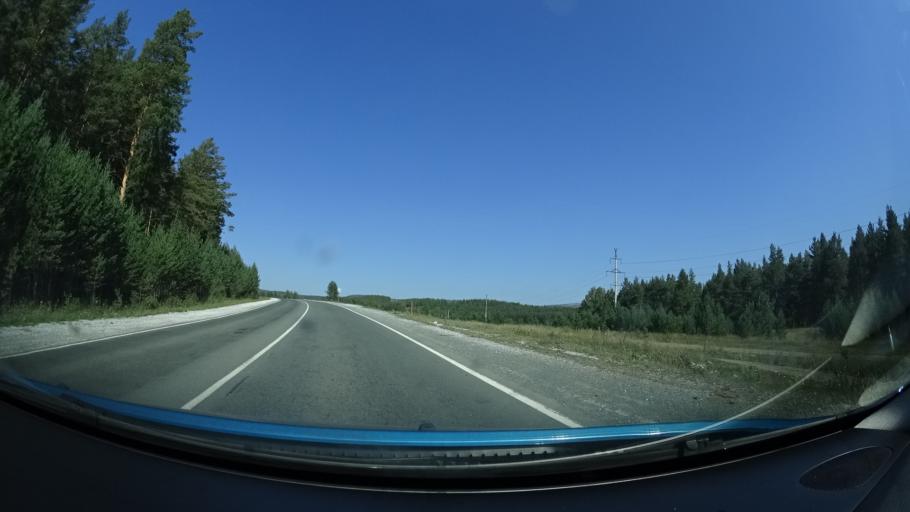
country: RU
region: Bashkortostan
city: Abzakovo
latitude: 53.8527
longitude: 58.5810
